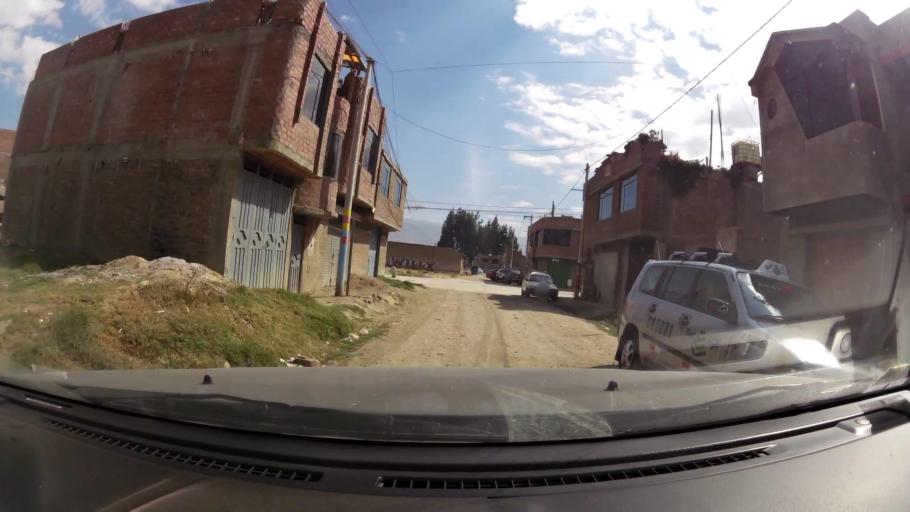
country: PE
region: Junin
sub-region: Provincia de Huancayo
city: Huancayo
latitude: -12.0958
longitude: -75.2022
